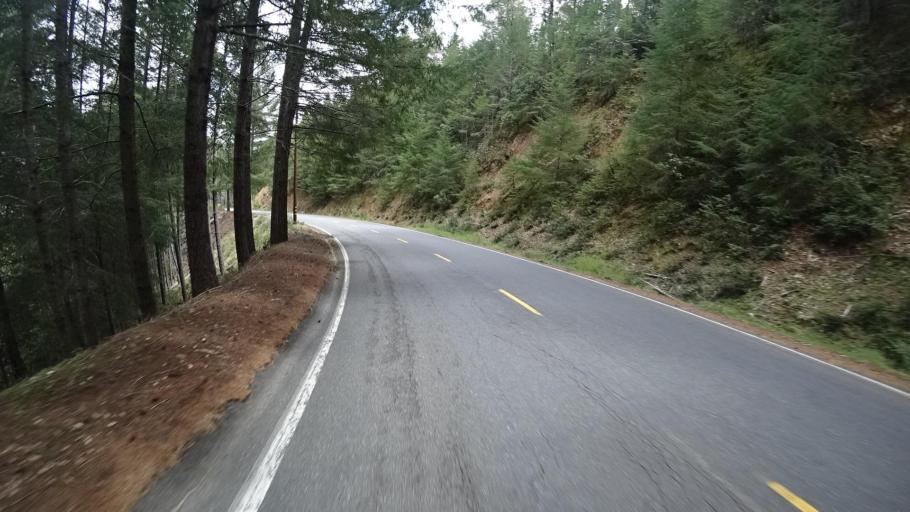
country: US
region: California
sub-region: Humboldt County
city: Redway
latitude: 40.0536
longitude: -123.9989
